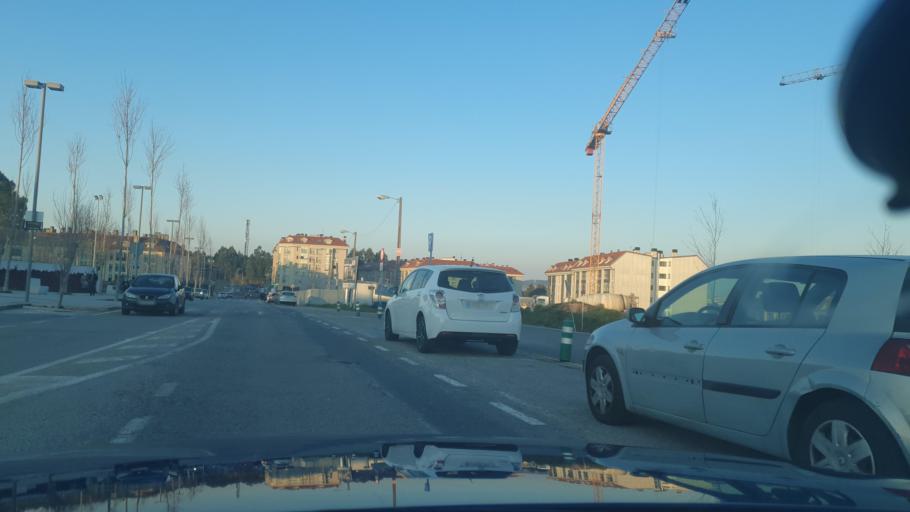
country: ES
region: Galicia
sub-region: Provincia da Coruna
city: Santiago de Compostela
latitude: 42.8451
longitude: -8.5806
